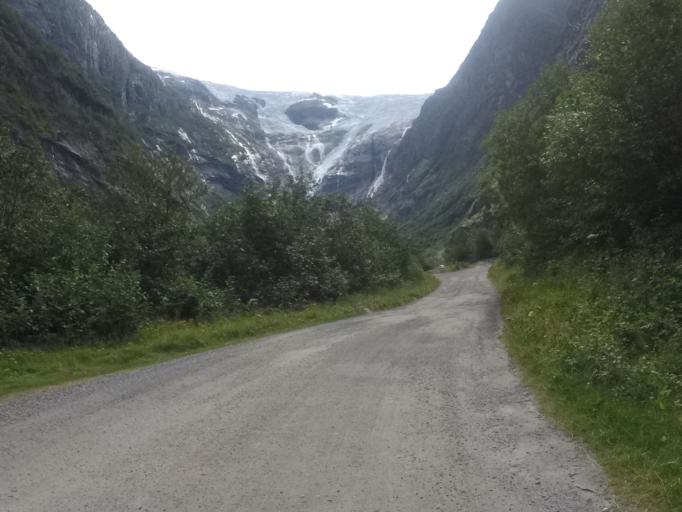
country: NO
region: Sogn og Fjordane
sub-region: Stryn
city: Stryn
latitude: 61.7566
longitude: 7.0376
